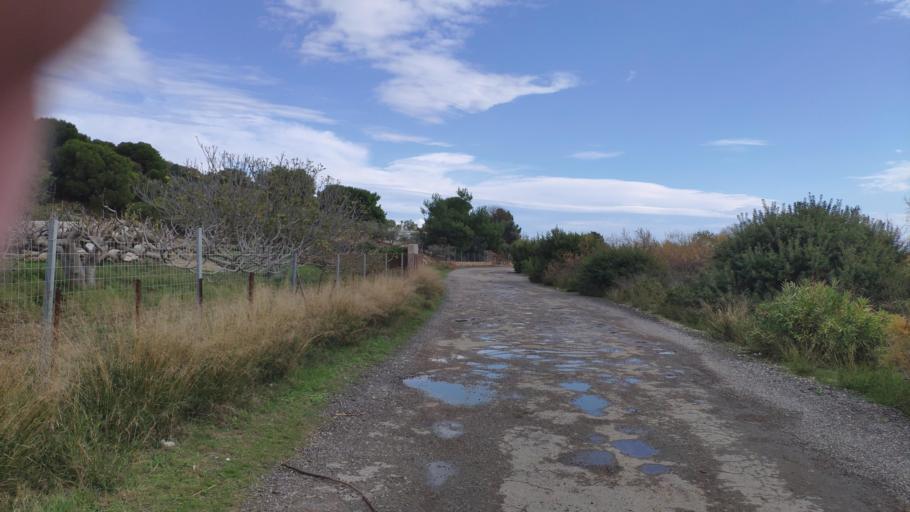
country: GR
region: Attica
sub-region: Nomarchia Anatolikis Attikis
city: Limin Mesoyaias
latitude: 37.9278
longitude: 24.0023
